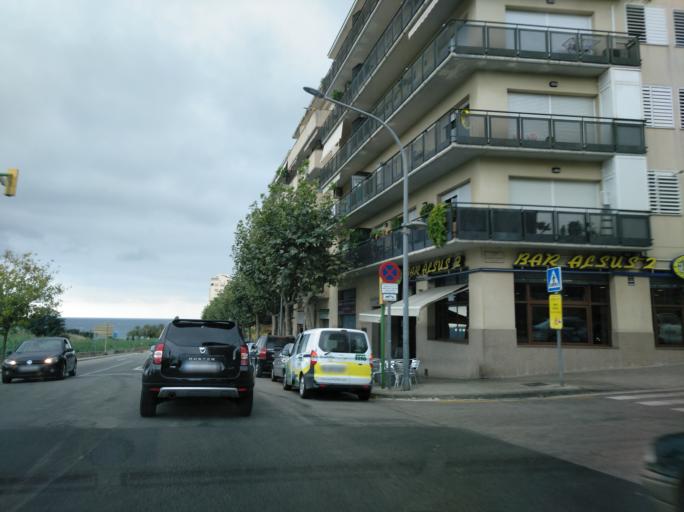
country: ES
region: Catalonia
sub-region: Provincia de Barcelona
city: Mataro
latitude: 41.5439
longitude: 2.4549
